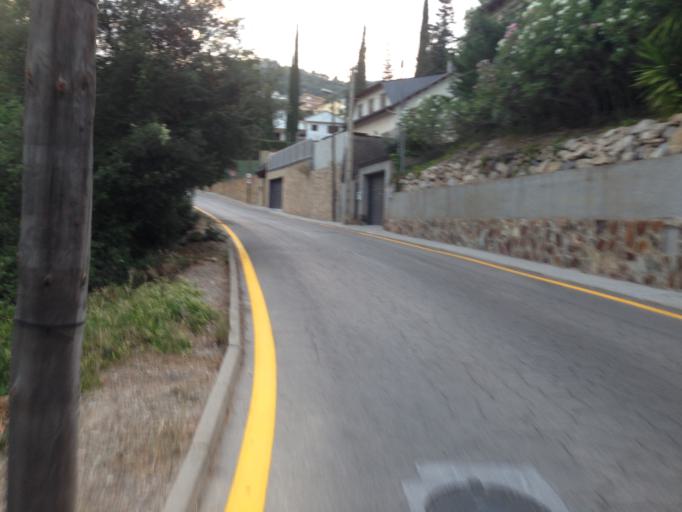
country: ES
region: Catalonia
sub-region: Provincia de Barcelona
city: Corbera de Llobregat
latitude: 41.4206
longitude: 1.9167
